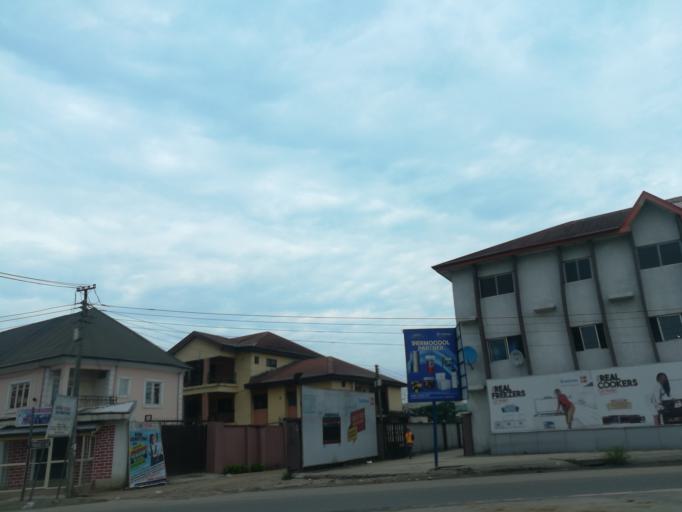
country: NG
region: Rivers
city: Port Harcourt
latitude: 4.8456
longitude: 6.9751
